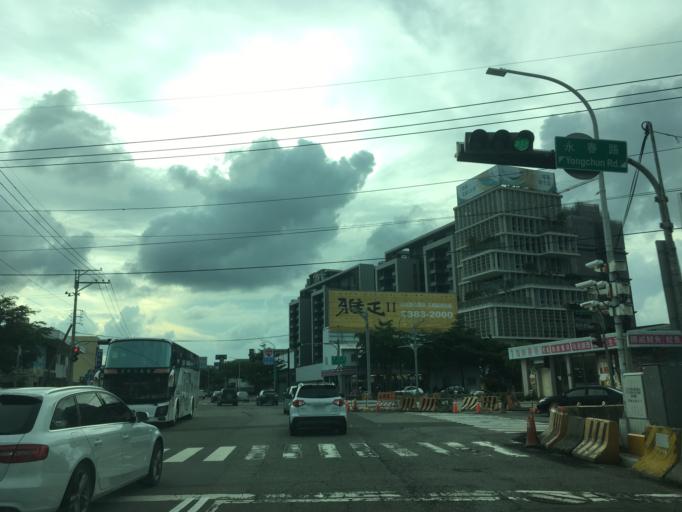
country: TW
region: Taiwan
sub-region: Taichung City
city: Taichung
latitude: 24.1400
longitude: 120.6290
